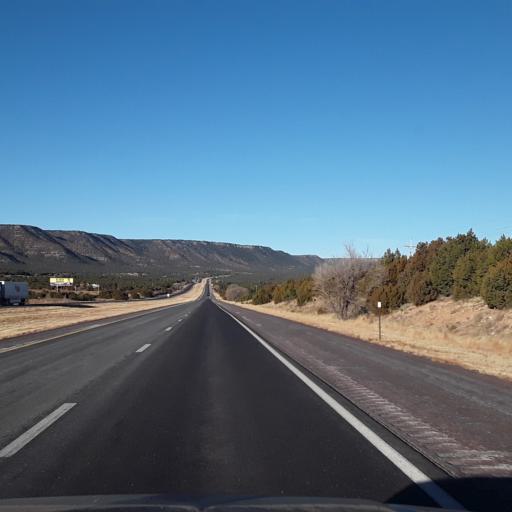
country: US
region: New Mexico
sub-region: San Miguel County
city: Pecos
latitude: 35.4222
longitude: -105.5574
